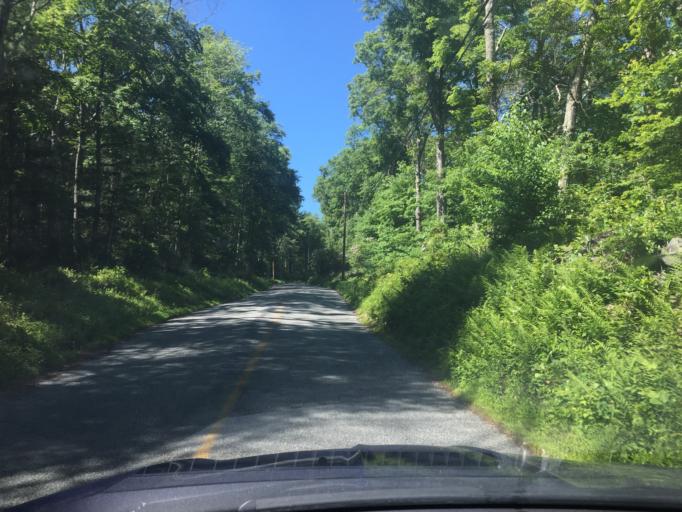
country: US
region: Rhode Island
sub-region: Washington County
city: Hopkinton
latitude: 41.4981
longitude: -71.8093
